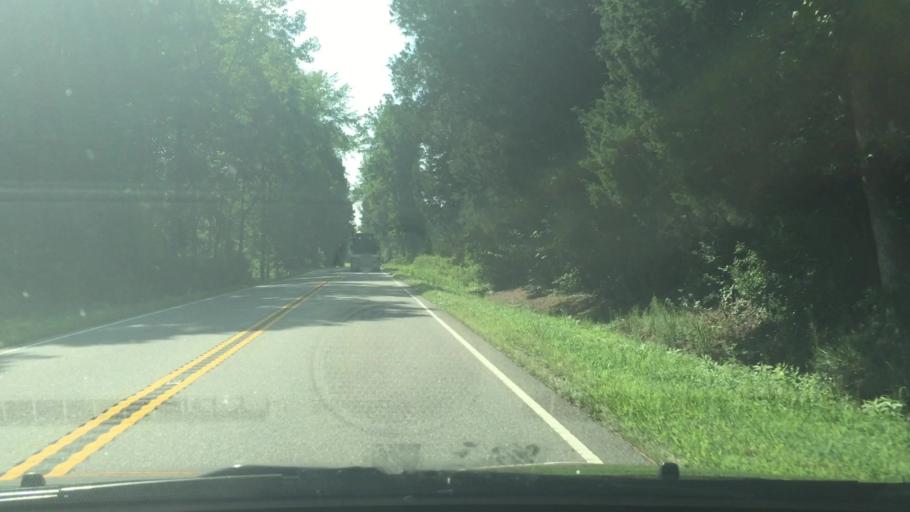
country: US
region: Virginia
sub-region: Sussex County
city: Sussex
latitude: 37.0218
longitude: -77.2877
